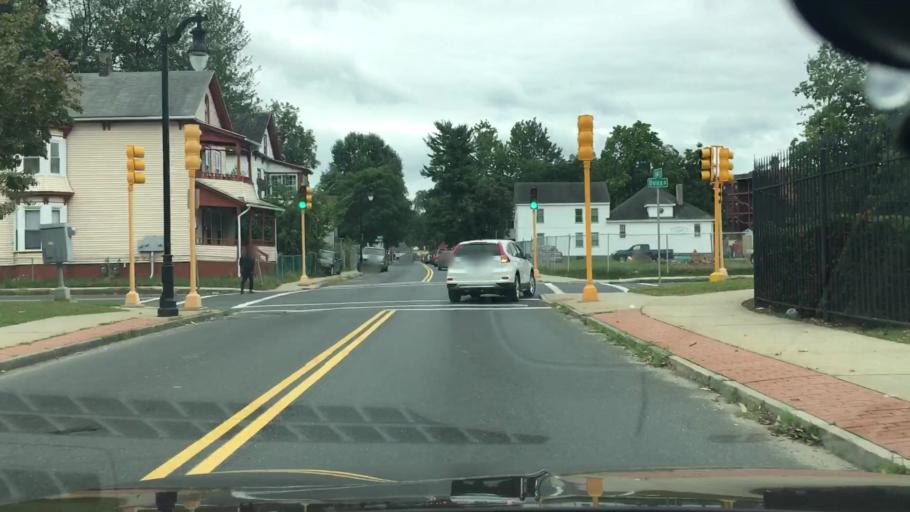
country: US
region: Massachusetts
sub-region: Hampden County
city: Springfield
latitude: 42.1077
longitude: -72.5739
